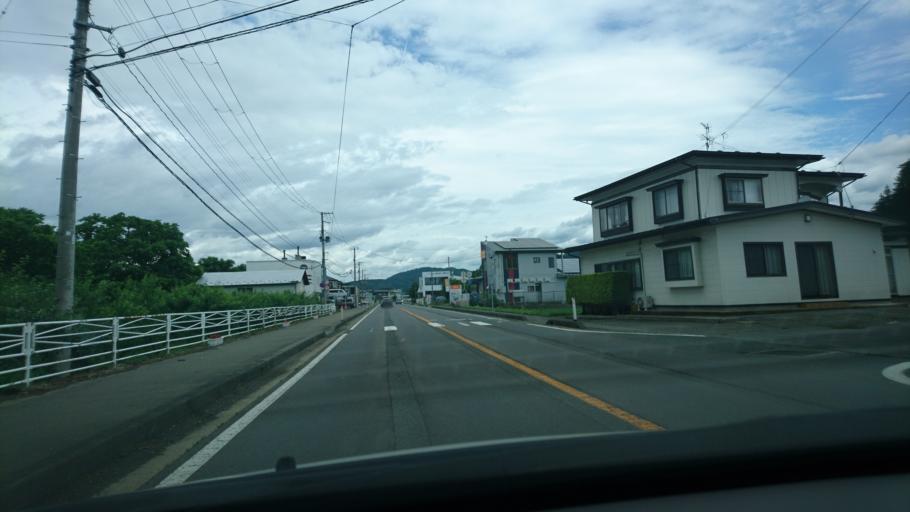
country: JP
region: Iwate
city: Morioka-shi
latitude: 39.6266
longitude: 141.1832
